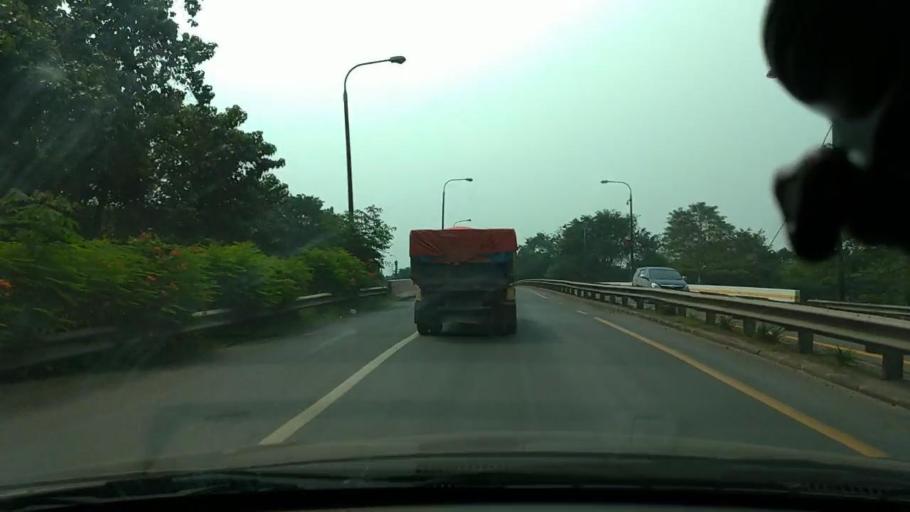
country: ID
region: Banten
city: Serang
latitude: -6.0890
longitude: 106.1449
